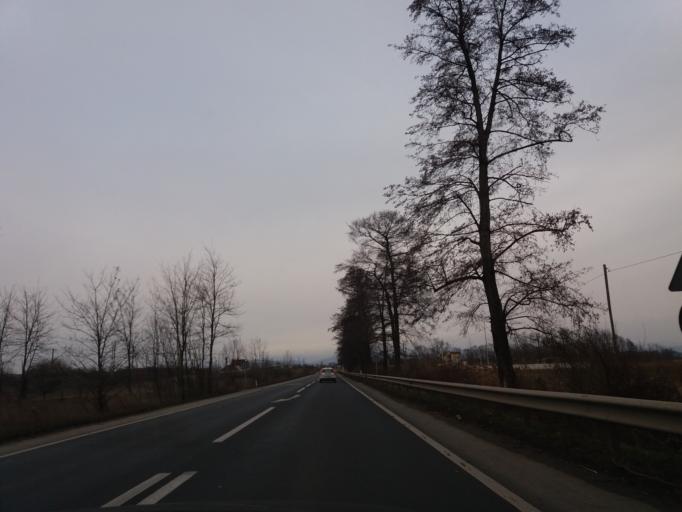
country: RO
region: Hunedoara
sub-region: Comuna Bacia
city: Bacia
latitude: 45.7919
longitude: 23.0013
